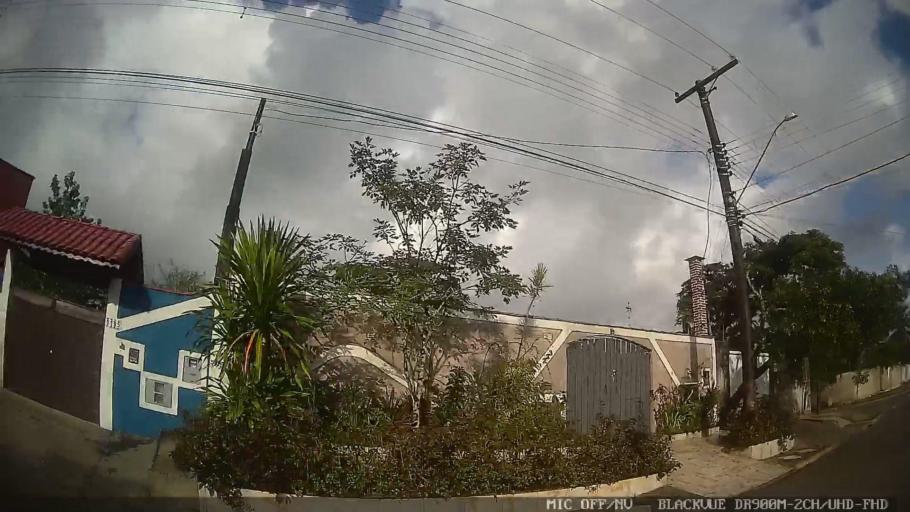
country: BR
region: Sao Paulo
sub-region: Itanhaem
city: Itanhaem
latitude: -24.1879
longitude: -46.8605
